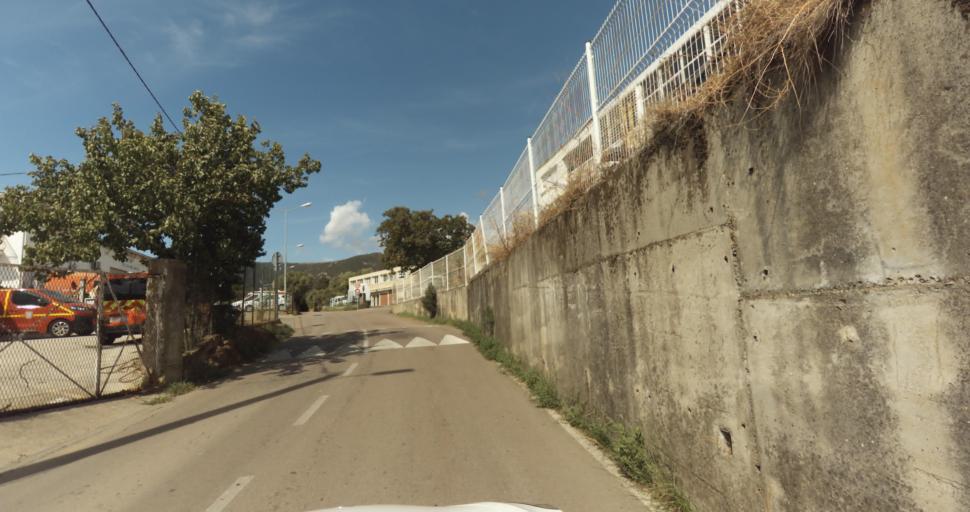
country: FR
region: Corsica
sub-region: Departement de la Corse-du-Sud
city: Afa
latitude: 41.9533
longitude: 8.7736
